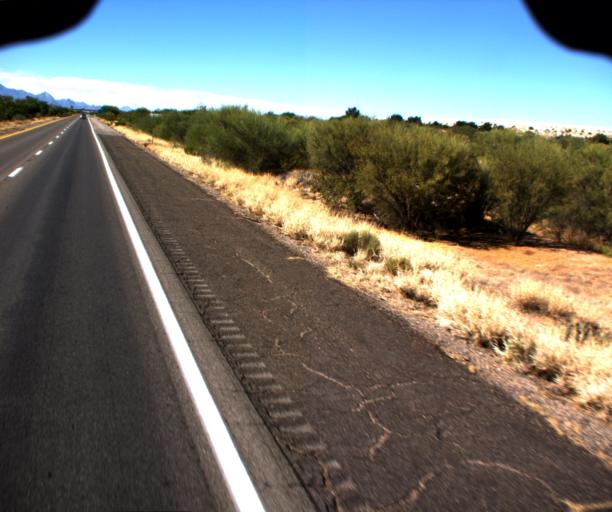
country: US
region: Arizona
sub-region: Pima County
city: Sahuarita
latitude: 31.9664
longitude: -110.9890
